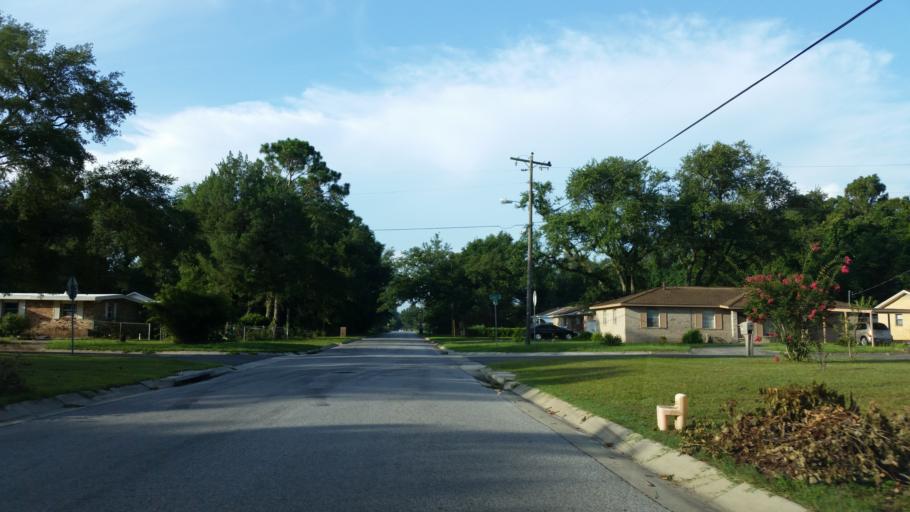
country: US
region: Florida
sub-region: Escambia County
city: Ferry Pass
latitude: 30.4942
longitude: -87.2009
